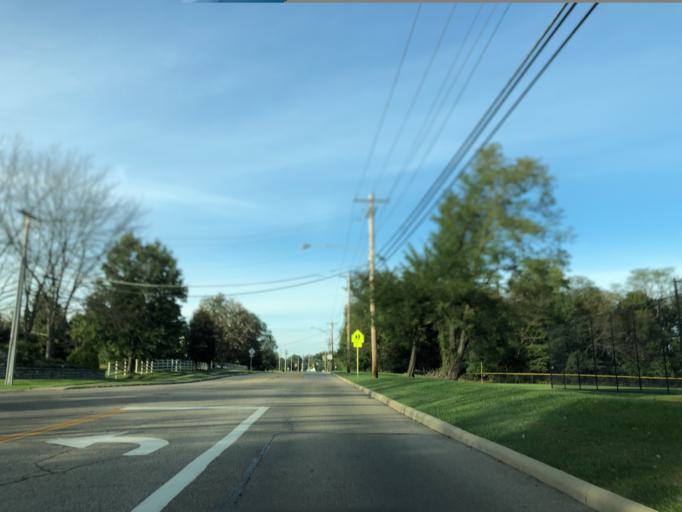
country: US
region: Ohio
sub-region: Hamilton County
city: Loveland
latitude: 39.2760
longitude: -84.2732
